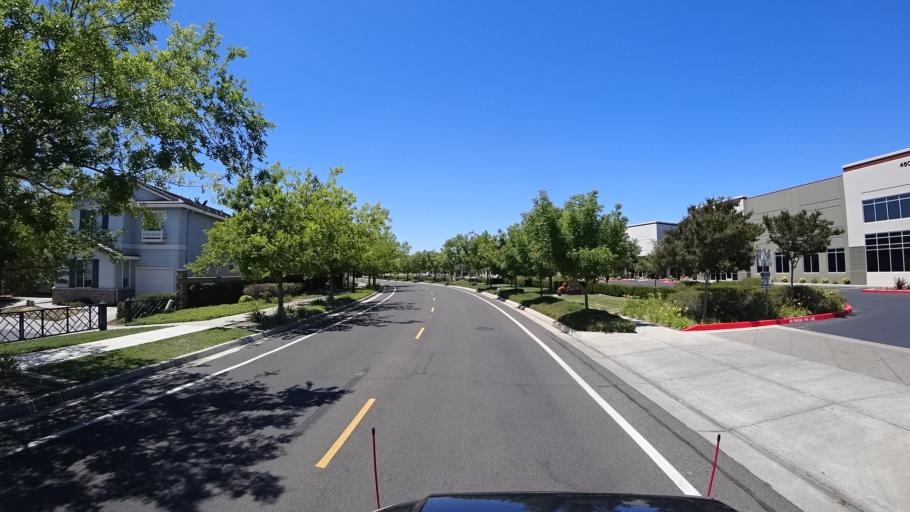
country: US
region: California
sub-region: Yolo County
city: West Sacramento
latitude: 38.6542
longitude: -121.5349
